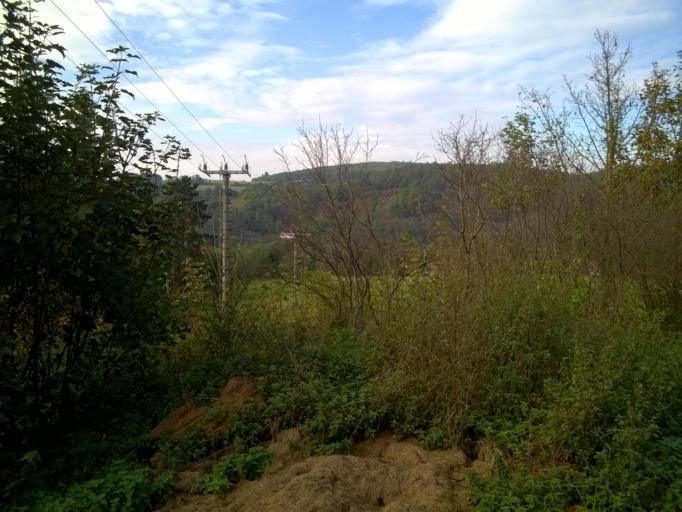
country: CZ
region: Central Bohemia
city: Kamenny Privoz
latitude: 49.8640
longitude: 14.4789
